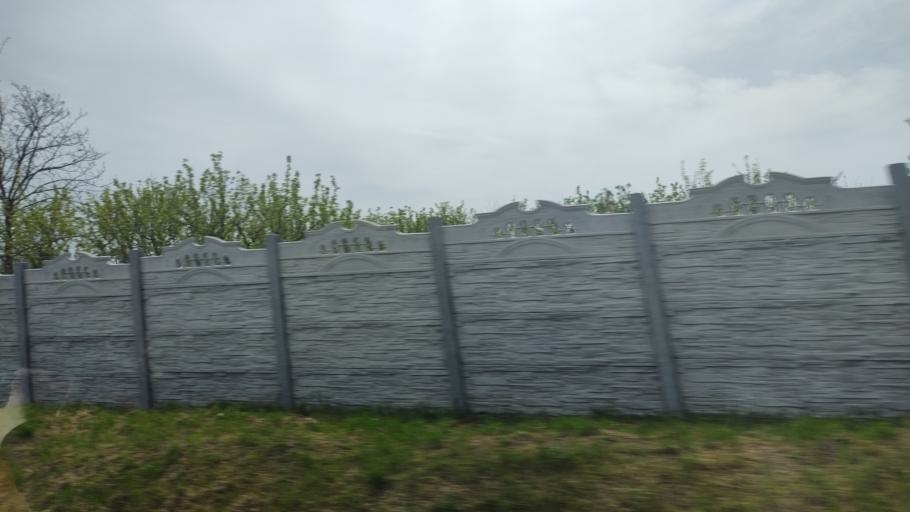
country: RO
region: Constanta
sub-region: Comuna Cobadin
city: Viisoara
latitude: 44.0770
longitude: 28.1995
